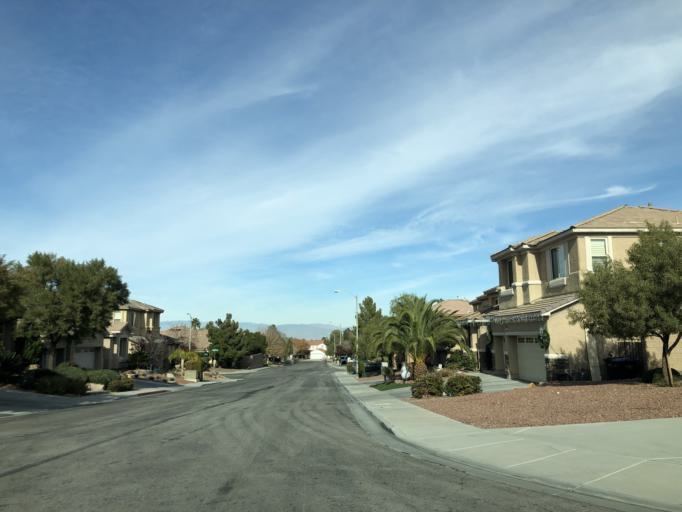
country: US
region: Nevada
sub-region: Clark County
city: Whitney
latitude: 36.0070
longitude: -115.0918
